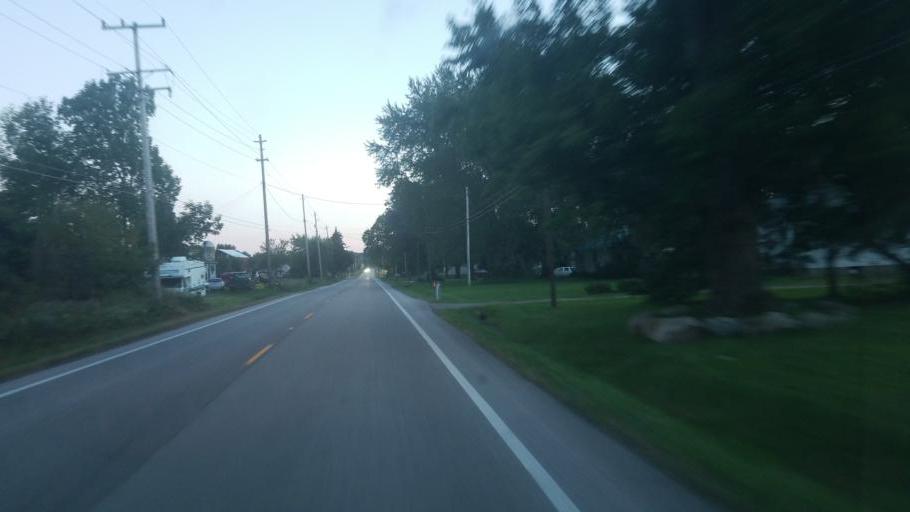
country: US
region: Ohio
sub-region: Ashtabula County
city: Andover
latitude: 41.7635
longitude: -80.5713
